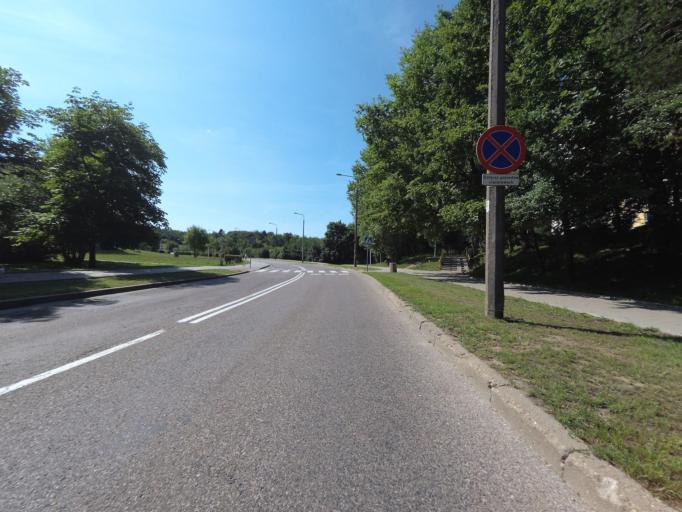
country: PL
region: Pomeranian Voivodeship
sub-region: Gdynia
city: Wielki Kack
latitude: 54.4940
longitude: 18.5077
